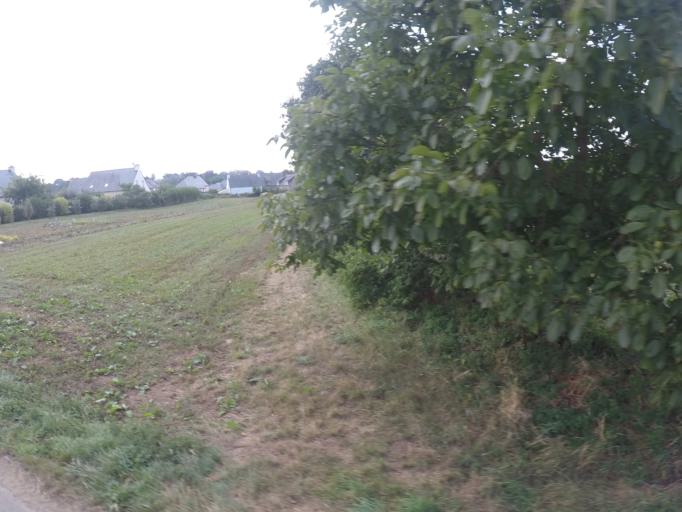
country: FR
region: Brittany
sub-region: Departement des Cotes-d'Armor
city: Plelo
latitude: 48.5588
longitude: -2.9521
